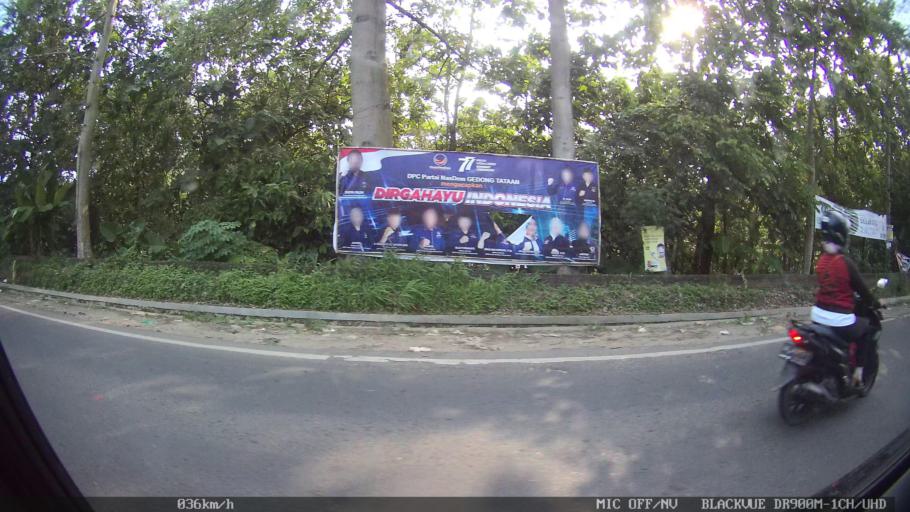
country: ID
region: Lampung
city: Kedaton
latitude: -5.3853
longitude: 105.2018
